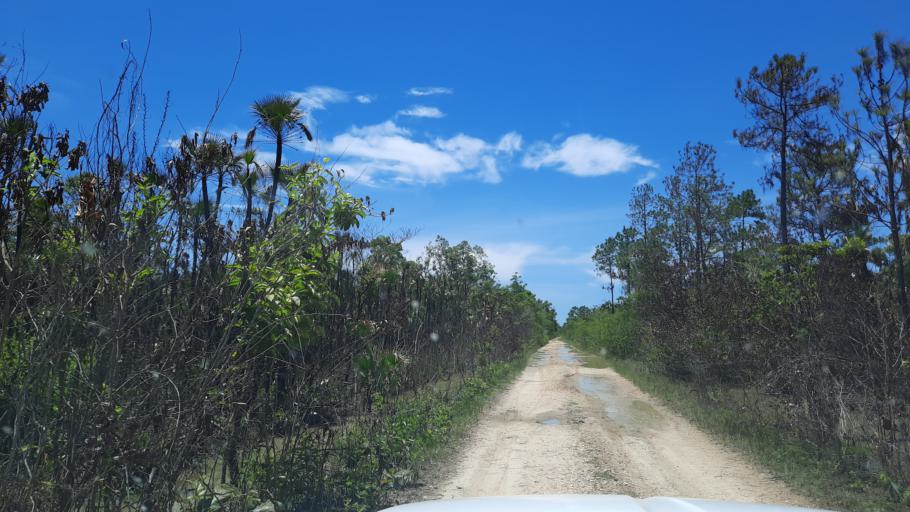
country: BZ
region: Cayo
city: Belmopan
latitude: 17.3766
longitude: -88.4880
